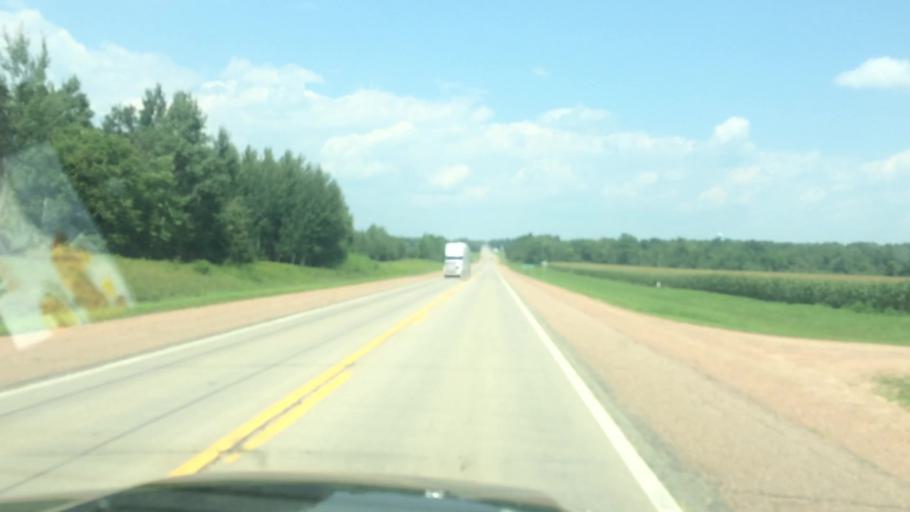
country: US
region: Wisconsin
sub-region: Clark County
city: Colby
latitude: 44.8842
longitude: -90.3155
